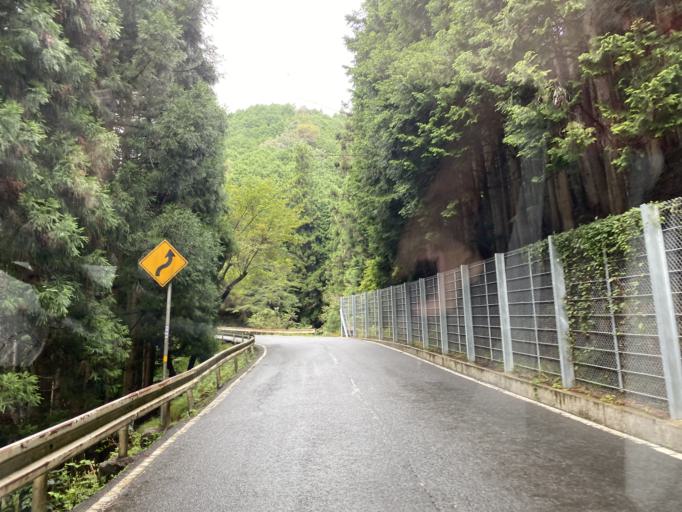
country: JP
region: Kyoto
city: Fukuchiyama
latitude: 35.3029
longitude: 134.9467
